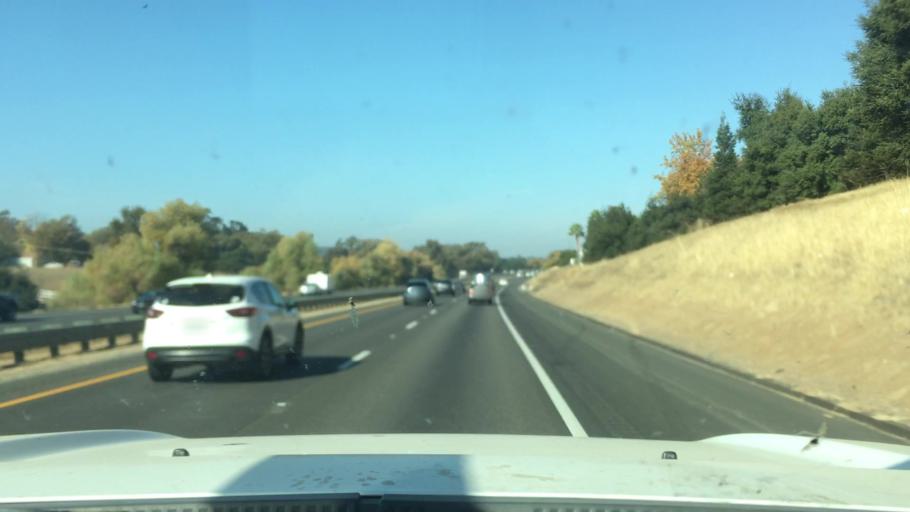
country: US
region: California
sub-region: San Luis Obispo County
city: Atascadero
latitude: 35.5014
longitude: -120.6890
